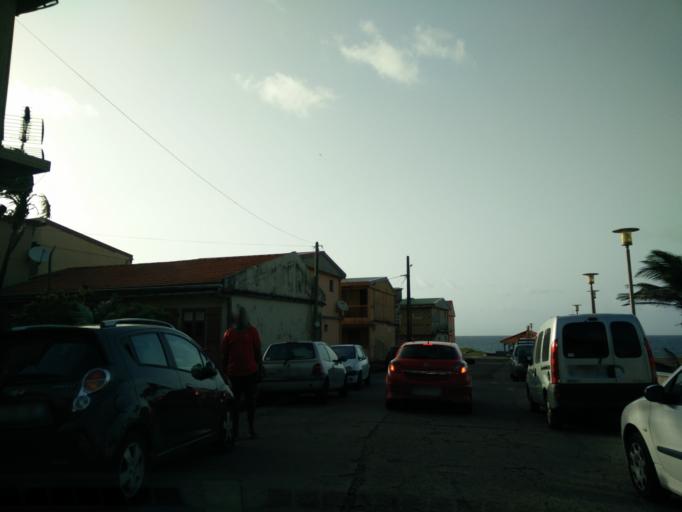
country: MQ
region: Martinique
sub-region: Martinique
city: Basse-Pointe
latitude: 14.8737
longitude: -61.1788
